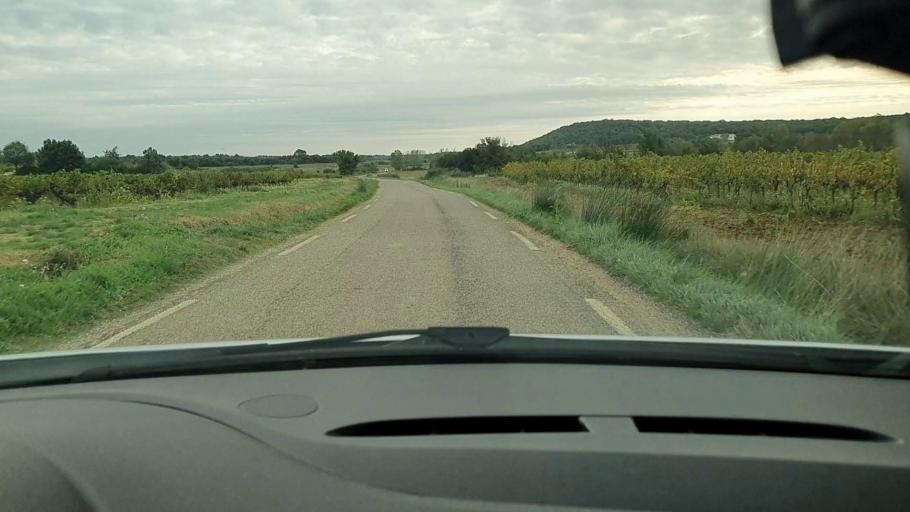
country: FR
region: Languedoc-Roussillon
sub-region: Departement du Gard
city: Saint-Chaptes
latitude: 44.0341
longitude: 4.2698
